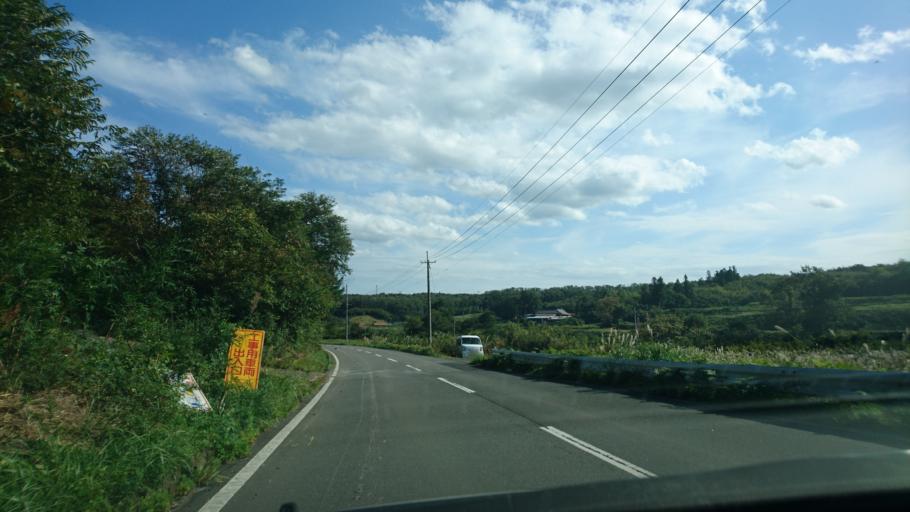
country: JP
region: Iwate
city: Ichinoseki
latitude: 38.8717
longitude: 141.0884
